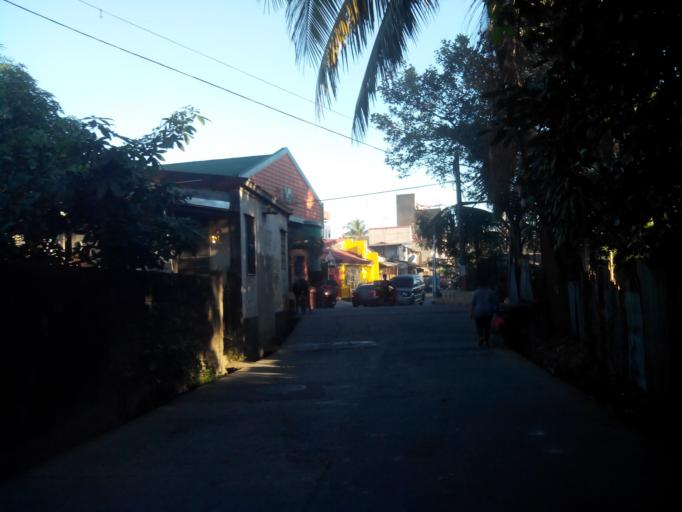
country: PH
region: Calabarzon
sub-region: Province of Rizal
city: Taytay
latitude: 14.5656
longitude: 121.1349
